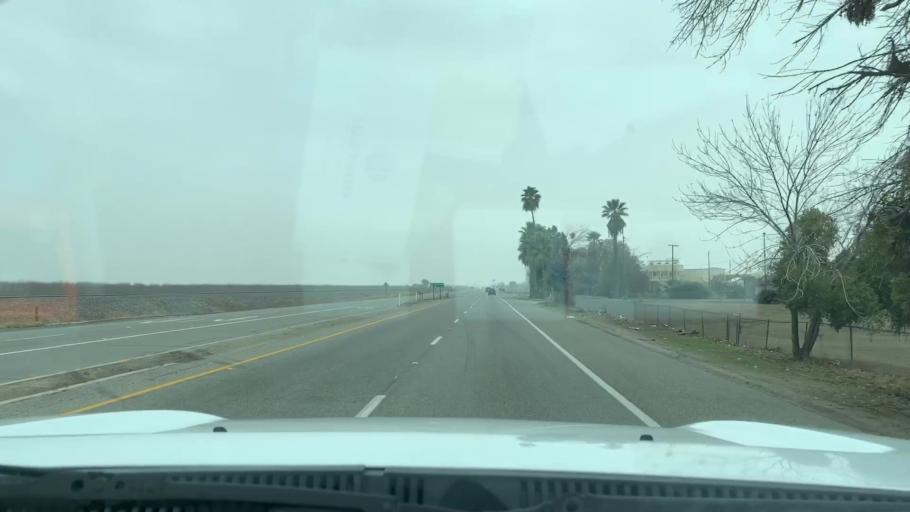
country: US
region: California
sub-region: Kern County
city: Shafter
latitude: 35.5287
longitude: -119.3058
